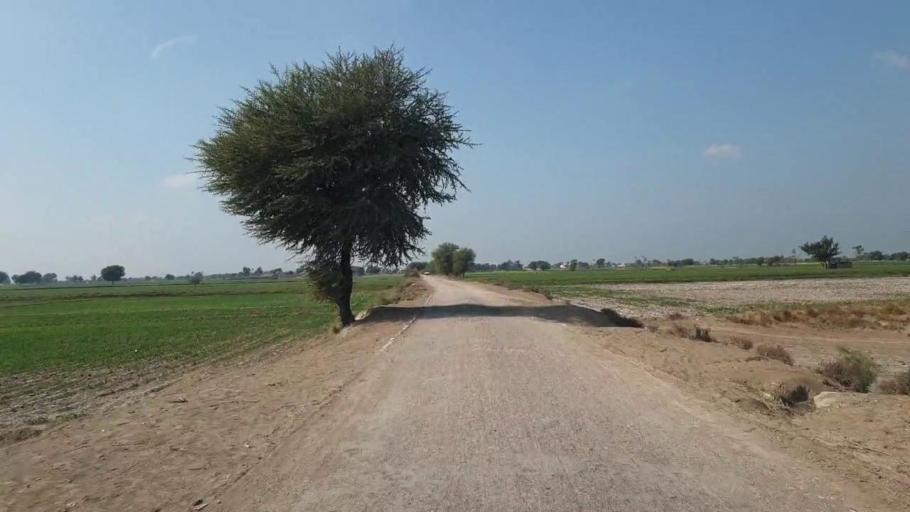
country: PK
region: Sindh
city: Shahdadpur
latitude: 26.0411
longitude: 68.5889
